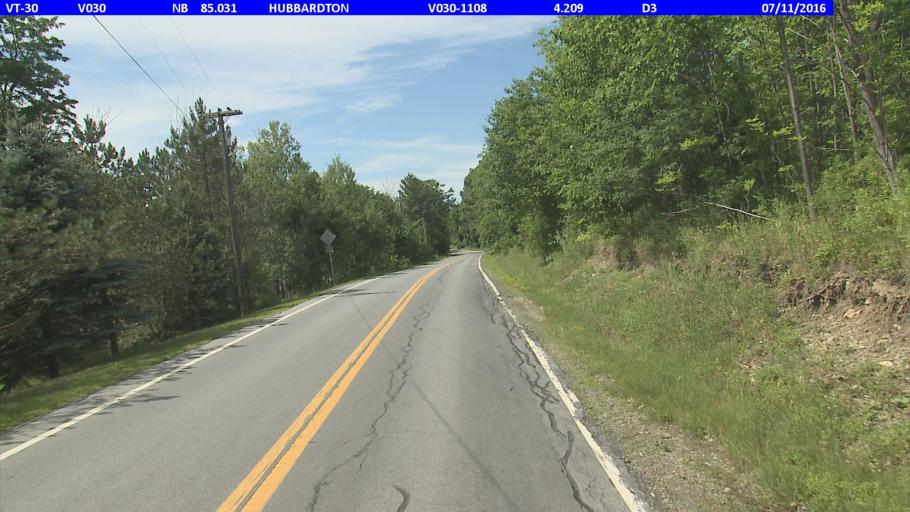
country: US
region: Vermont
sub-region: Rutland County
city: Brandon
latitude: 43.7380
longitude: -73.1810
